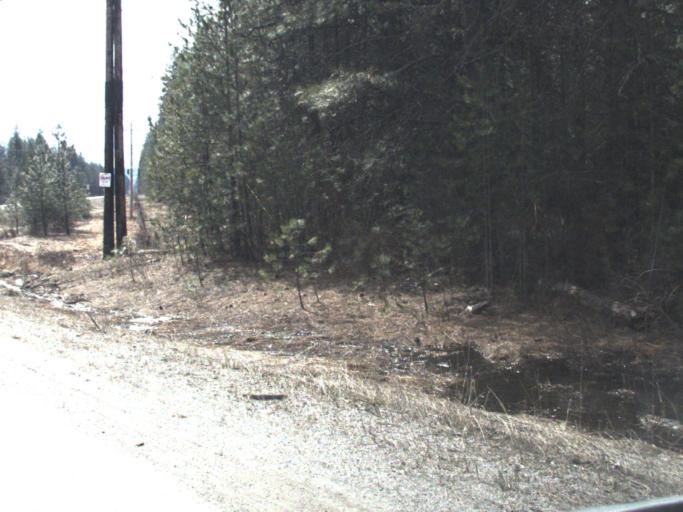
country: US
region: Washington
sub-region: Pend Oreille County
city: Newport
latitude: 48.3059
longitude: -117.2844
